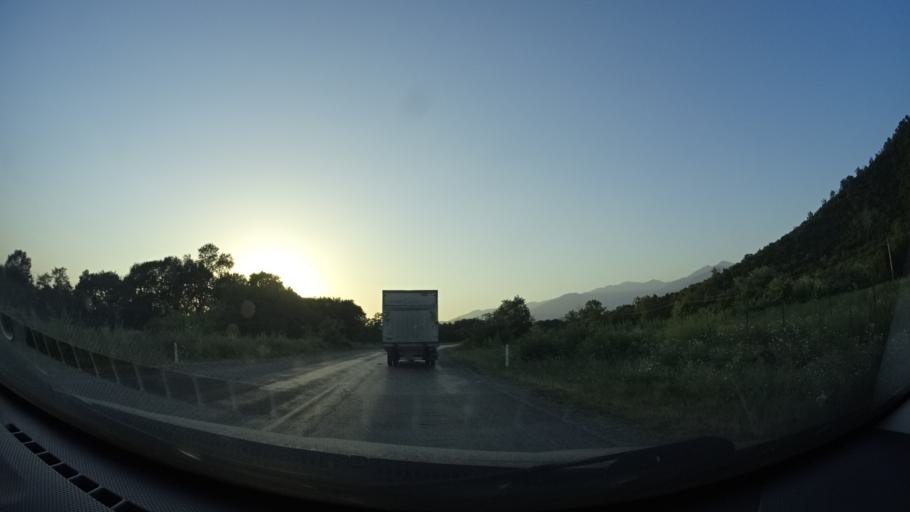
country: GE
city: Bagdadi
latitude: 41.8551
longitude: 46.0298
